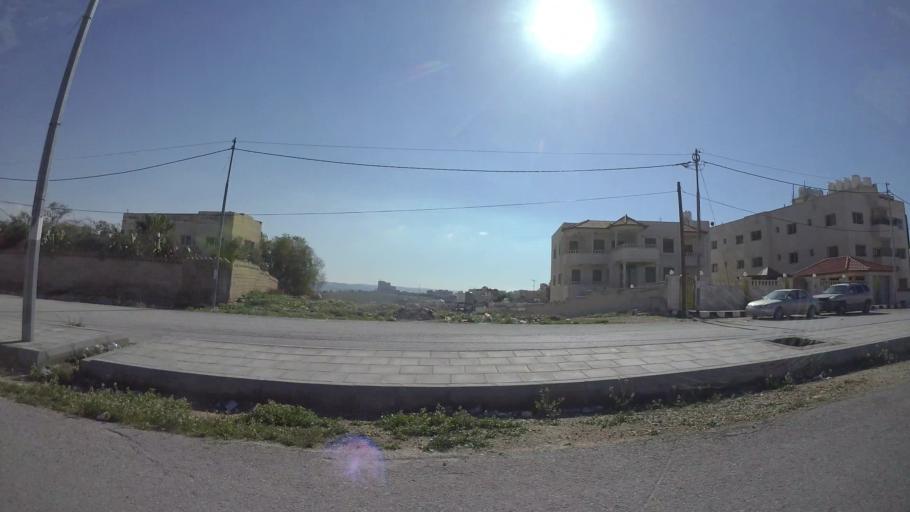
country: JO
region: Zarqa
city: Russeifa
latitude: 32.0415
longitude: 36.0517
